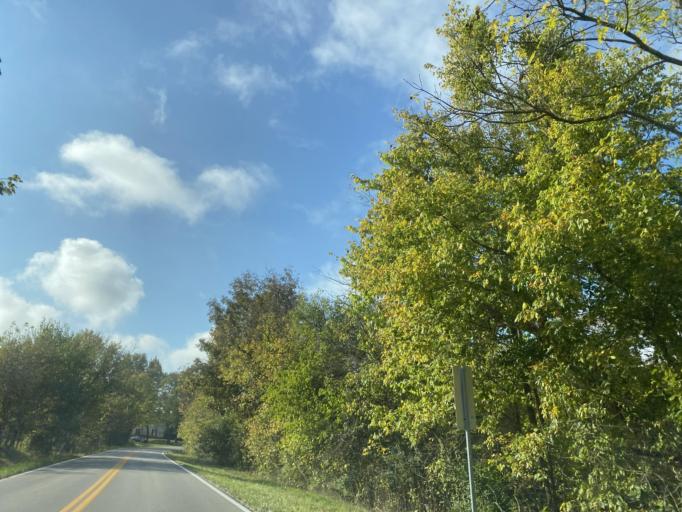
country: US
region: Kentucky
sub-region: Pendleton County
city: Falmouth
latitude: 38.7051
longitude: -84.3041
